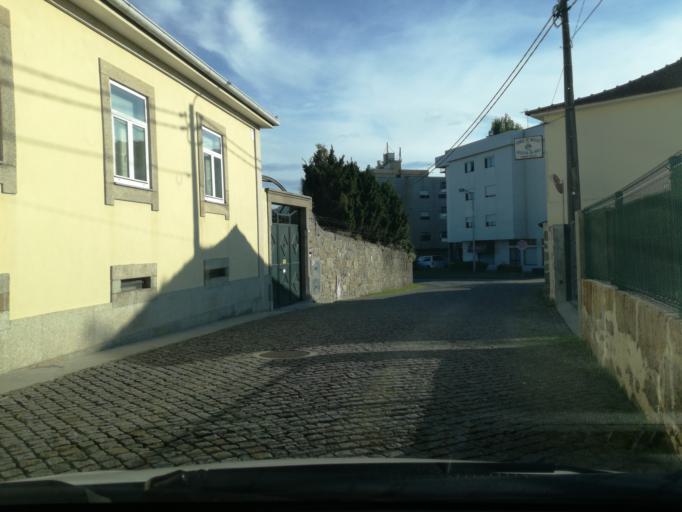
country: PT
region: Porto
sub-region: Maia
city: Gemunde
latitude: 41.2507
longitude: -8.6481
